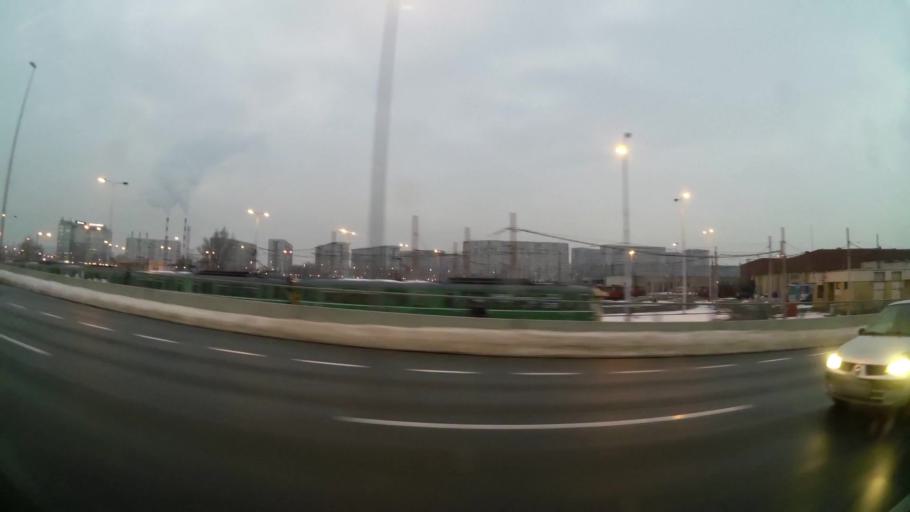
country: RS
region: Central Serbia
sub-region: Belgrade
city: Novi Beograd
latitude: 44.8091
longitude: 20.4113
